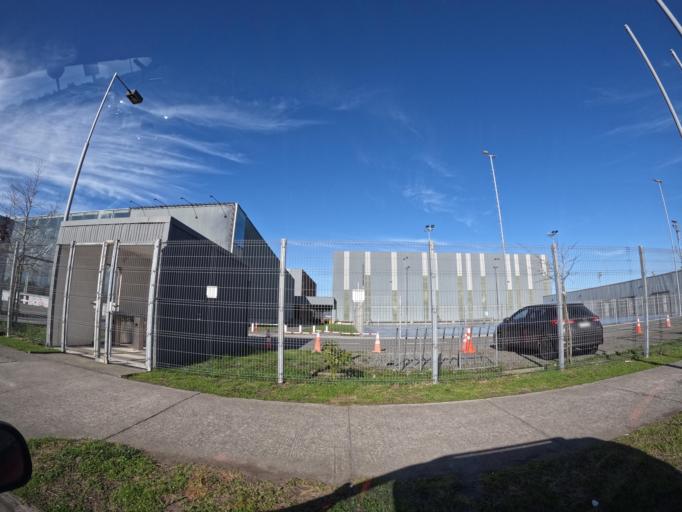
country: CL
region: Biobio
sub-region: Provincia de Concepcion
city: Concepcion
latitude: -36.7722
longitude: -73.0667
